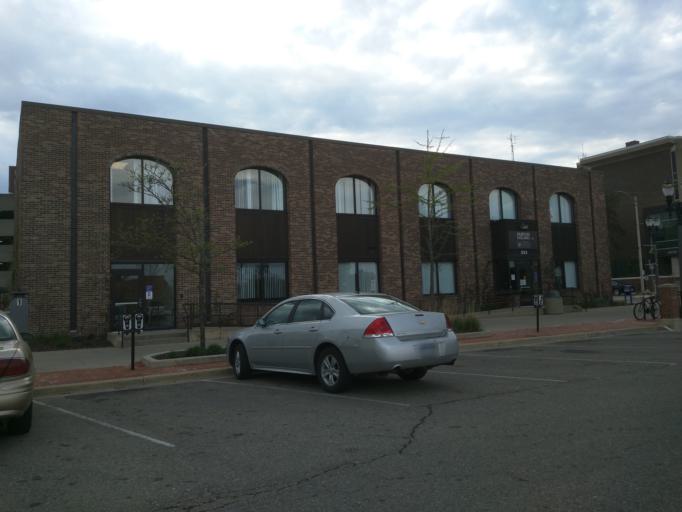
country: US
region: Michigan
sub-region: Ingham County
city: Lansing
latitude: 42.7368
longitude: -84.5524
